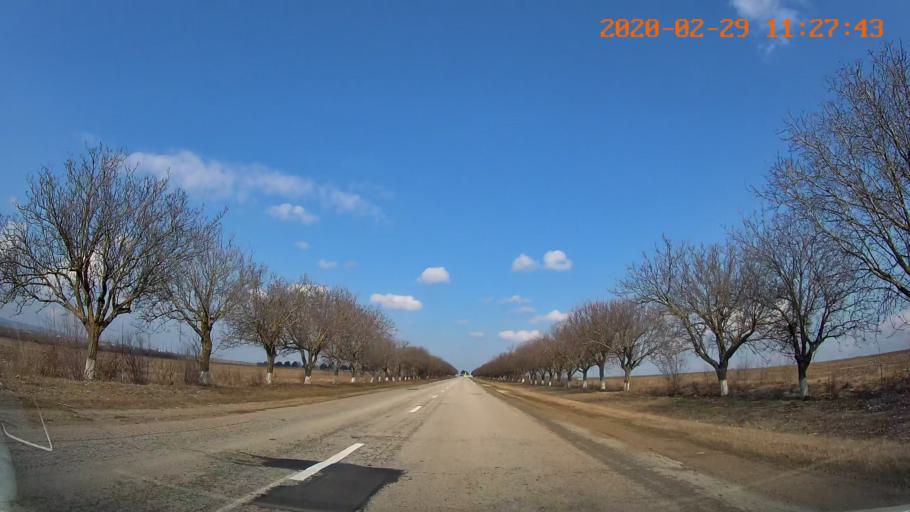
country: MD
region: Telenesti
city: Cocieri
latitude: 47.4727
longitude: 29.1413
